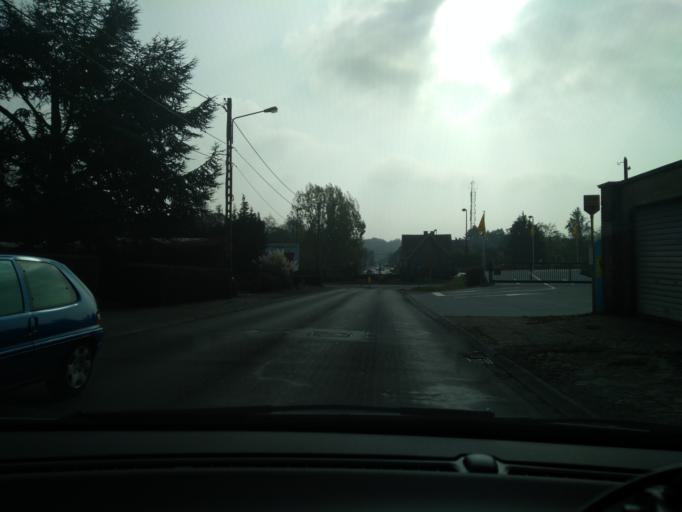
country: BE
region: Wallonia
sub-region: Province du Hainaut
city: Colfontaine
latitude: 50.4270
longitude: 3.8409
